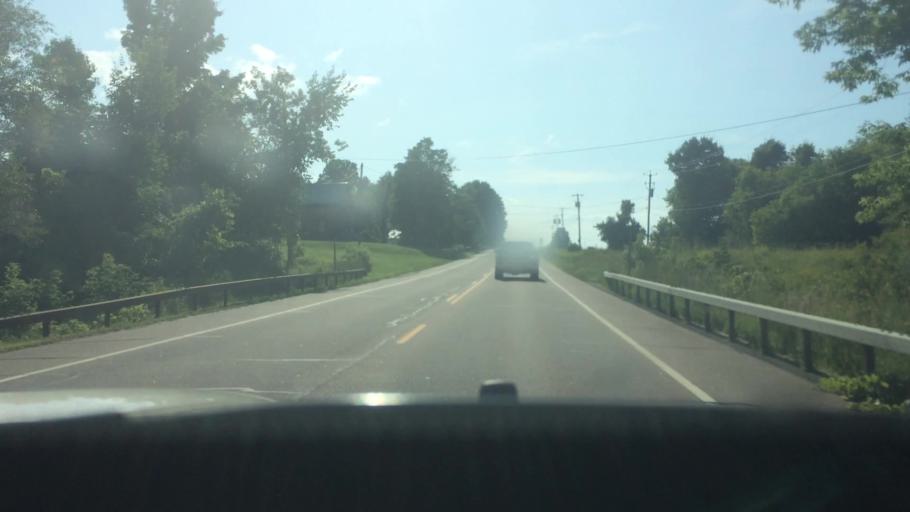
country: US
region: New York
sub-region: Franklin County
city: Malone
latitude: 44.8589
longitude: -74.2509
